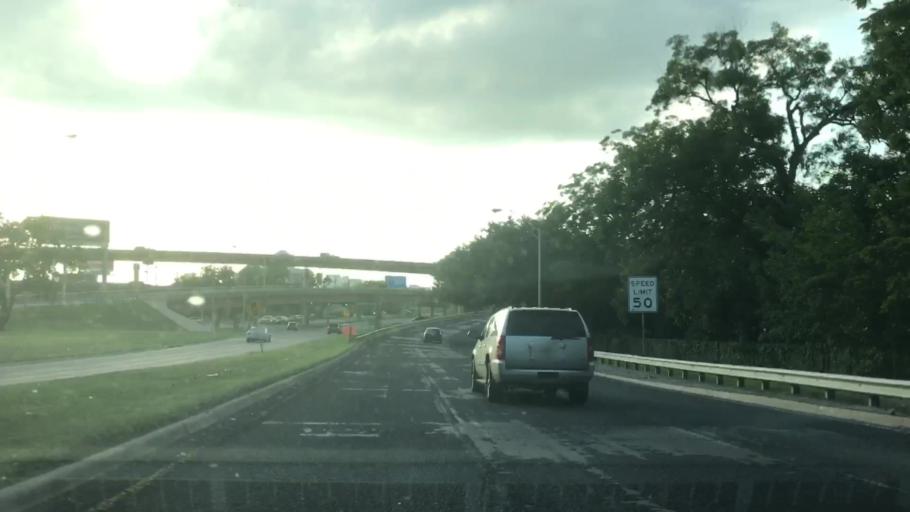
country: US
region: Texas
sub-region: Dallas County
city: Dallas
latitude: 32.7982
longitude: -96.8129
